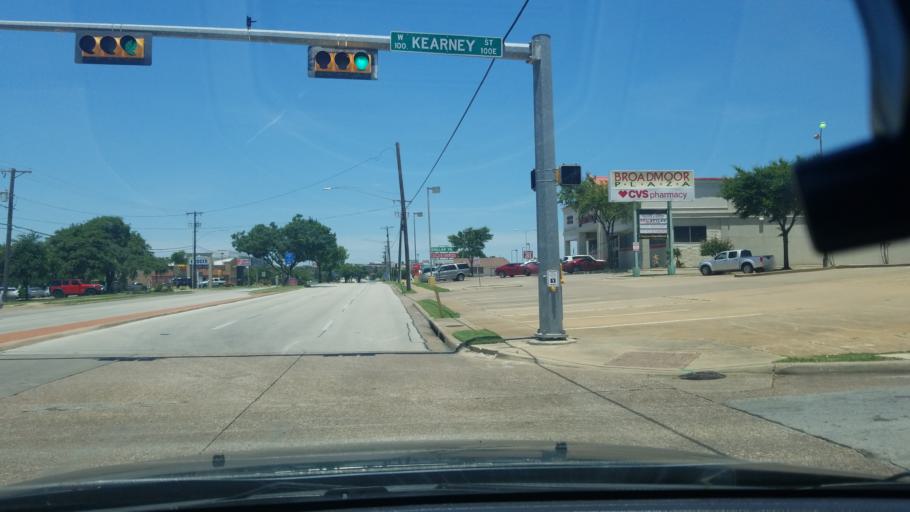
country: US
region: Texas
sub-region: Dallas County
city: Mesquite
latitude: 32.7708
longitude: -96.5990
